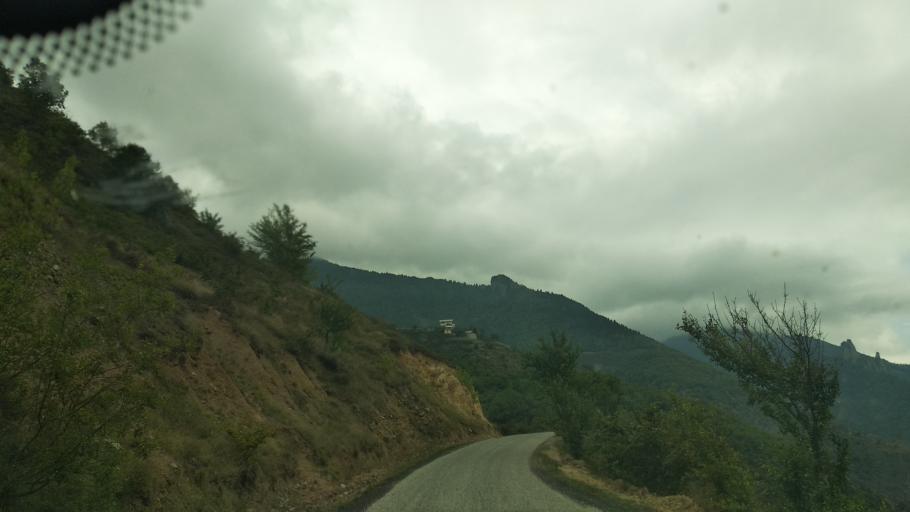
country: TR
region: Giresun
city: Dogankent
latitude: 40.7400
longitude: 38.9895
